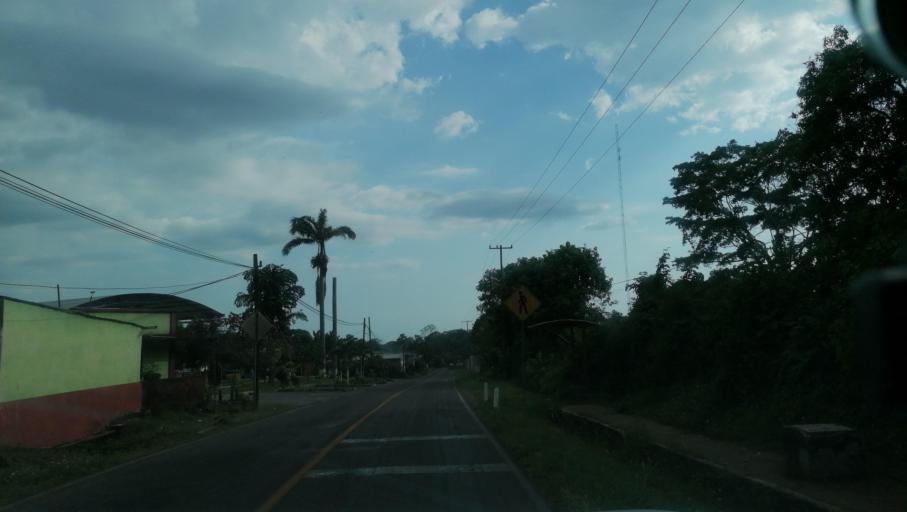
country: MX
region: Chiapas
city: Cacahoatan
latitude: 15.0088
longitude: -92.1558
